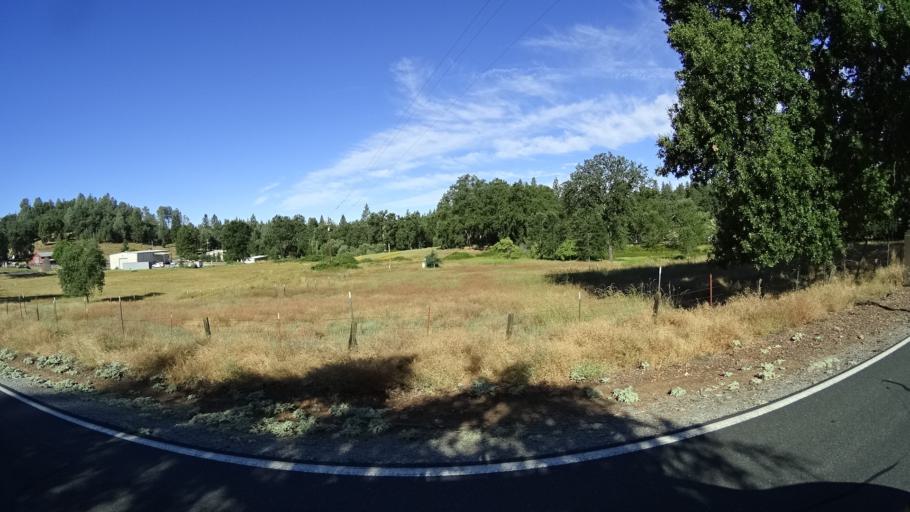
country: US
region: California
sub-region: Amador County
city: Pioneer
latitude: 38.3813
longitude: -120.5327
